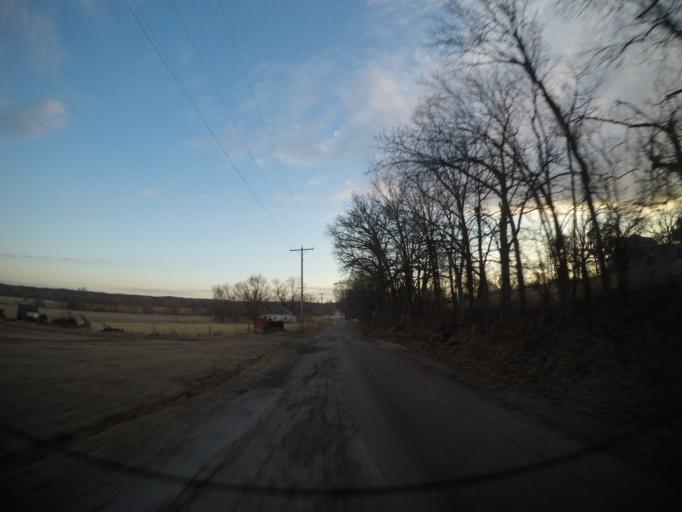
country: US
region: Kansas
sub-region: Wyandotte County
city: Bonner Springs
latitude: 39.0168
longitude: -94.9088
